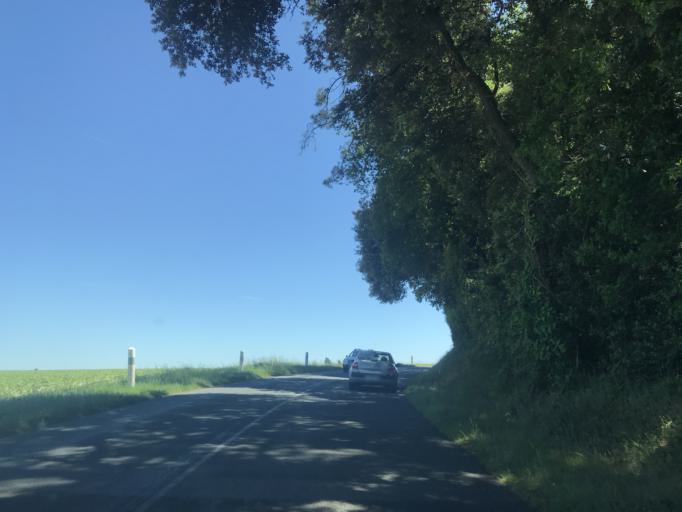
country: FR
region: Poitou-Charentes
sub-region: Departement de la Charente-Maritime
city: Meschers-sur-Gironde
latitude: 45.5921
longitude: -0.9656
